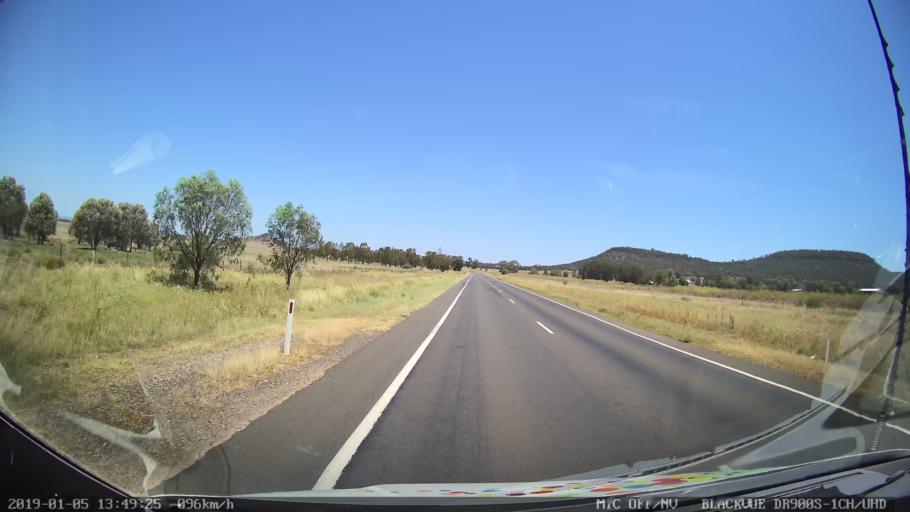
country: AU
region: New South Wales
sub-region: Gunnedah
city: Gunnedah
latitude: -31.0156
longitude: 150.2737
